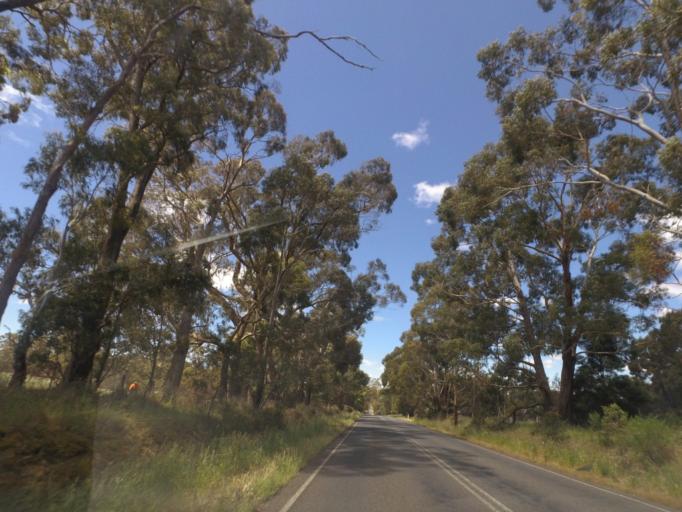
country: AU
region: Victoria
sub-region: Mount Alexander
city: Castlemaine
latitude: -37.3189
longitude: 144.2102
